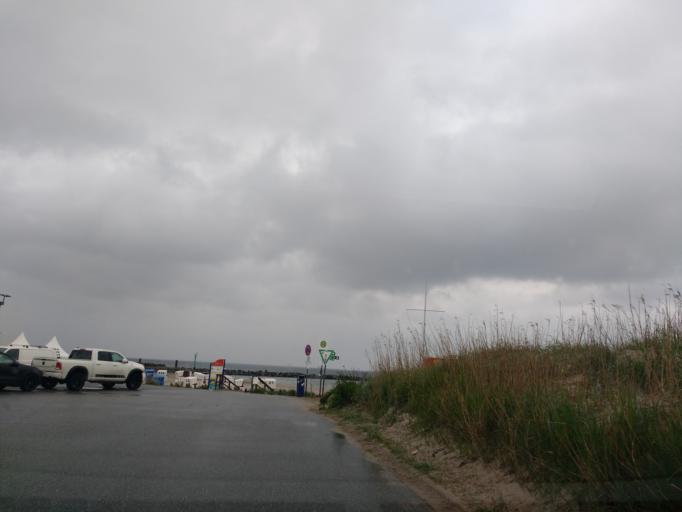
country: DE
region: Schleswig-Holstein
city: Damp
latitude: 54.5810
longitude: 10.0248
